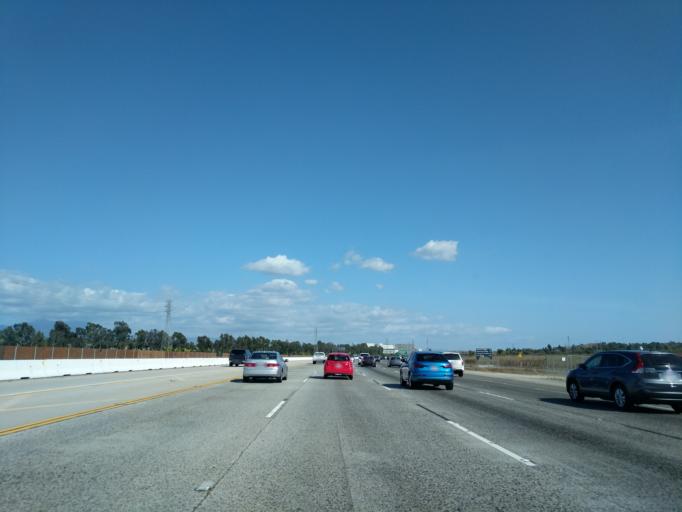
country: US
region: California
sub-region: Orange County
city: Irvine
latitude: 33.6623
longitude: -117.7886
